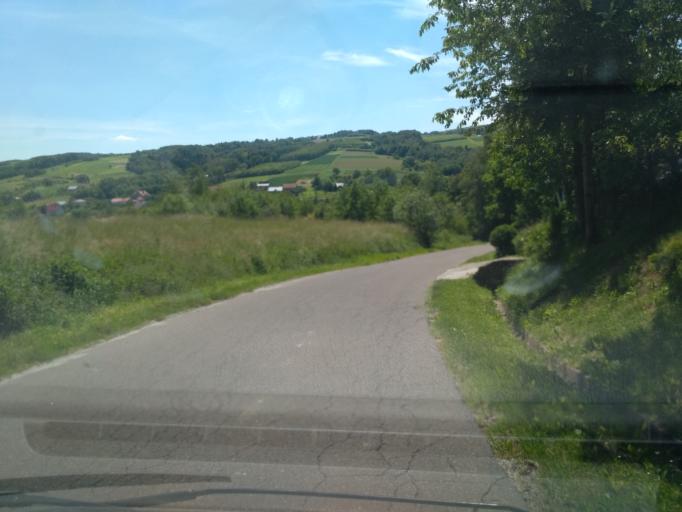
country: PL
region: Subcarpathian Voivodeship
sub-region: Powiat strzyzowski
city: Polomia
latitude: 49.9019
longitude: 21.8858
